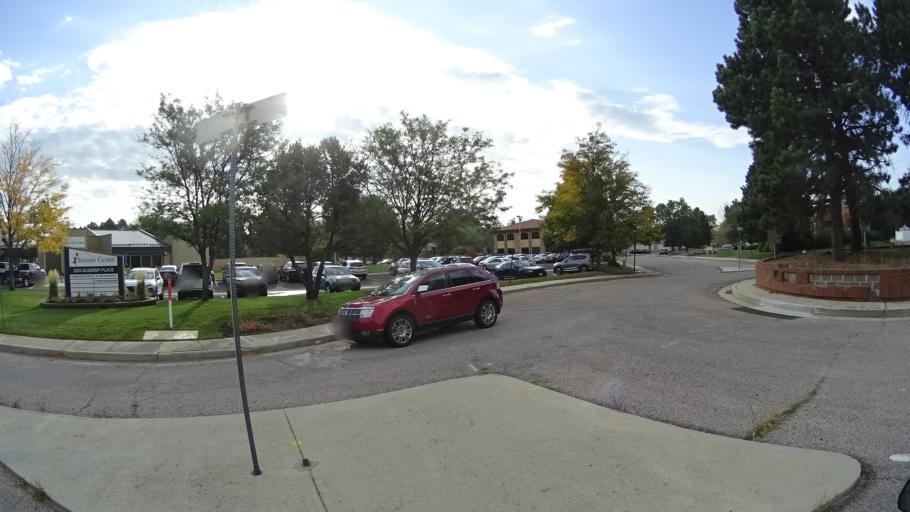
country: US
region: Colorado
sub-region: El Paso County
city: Cimarron Hills
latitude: 38.8647
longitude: -104.7557
